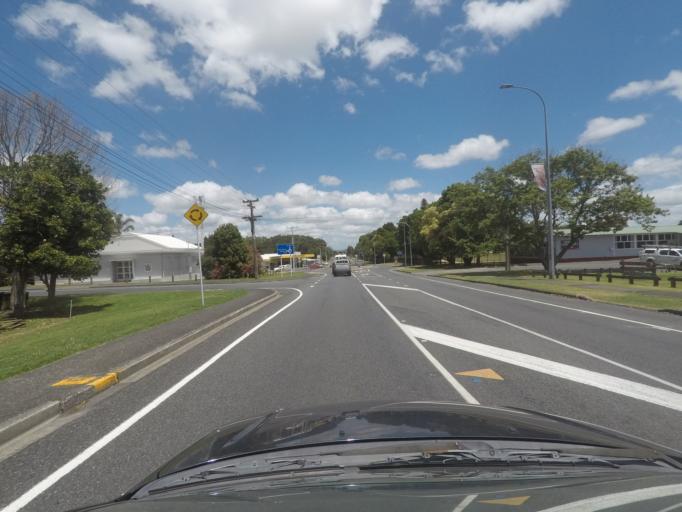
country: NZ
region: Northland
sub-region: Whangarei
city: Whangarei
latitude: -35.7564
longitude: 174.3684
